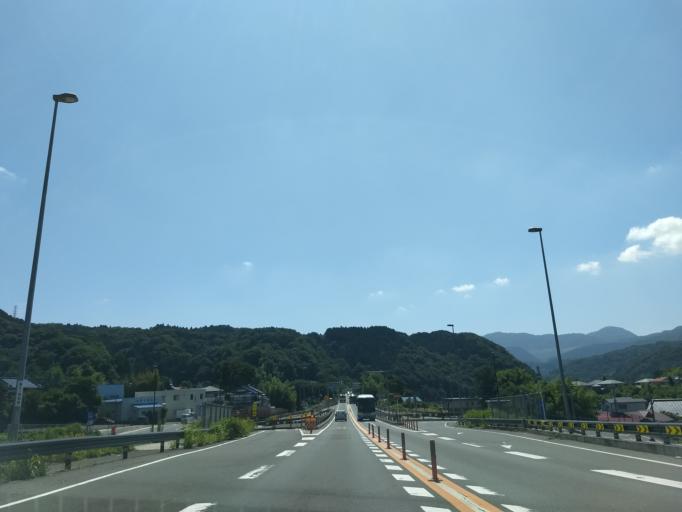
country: JP
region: Shizuoka
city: Gotemba
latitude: 35.3675
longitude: 138.9820
